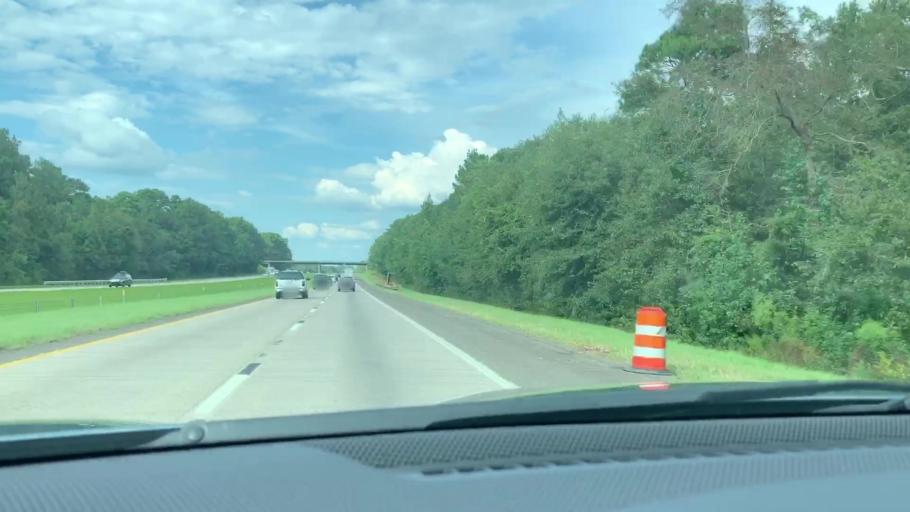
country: US
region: South Carolina
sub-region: Hampton County
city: Yemassee
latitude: 32.6746
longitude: -80.8827
